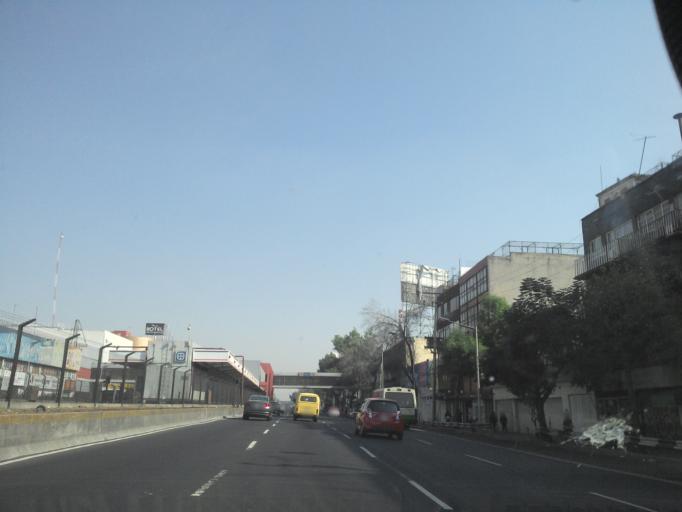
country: MX
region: Mexico City
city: Colonia Nativitas
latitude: 19.3995
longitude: -99.1370
